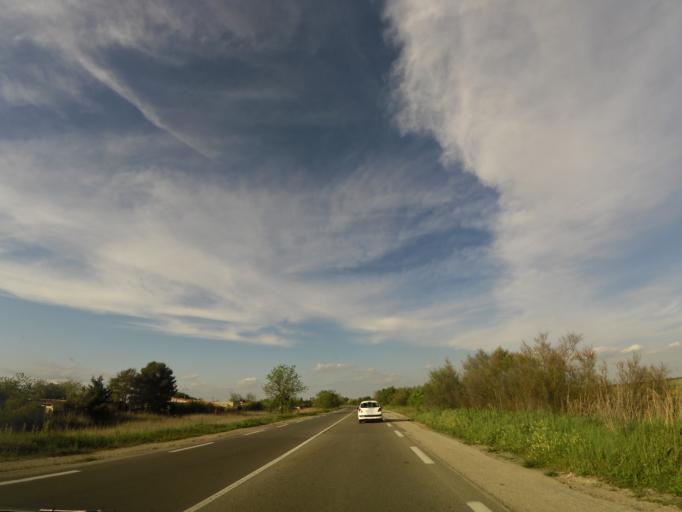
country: FR
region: Languedoc-Roussillon
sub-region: Departement de l'Herault
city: Candillargues
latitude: 43.6105
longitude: 4.1091
